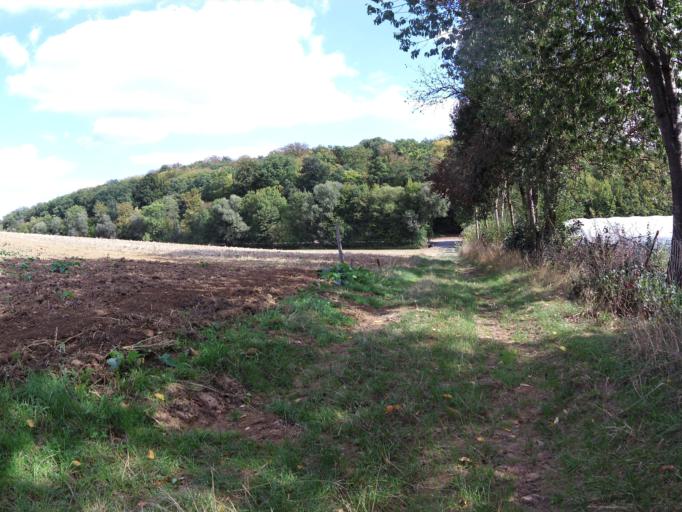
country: DE
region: Bavaria
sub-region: Regierungsbezirk Unterfranken
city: Hettstadt
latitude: 49.7898
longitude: 9.8028
